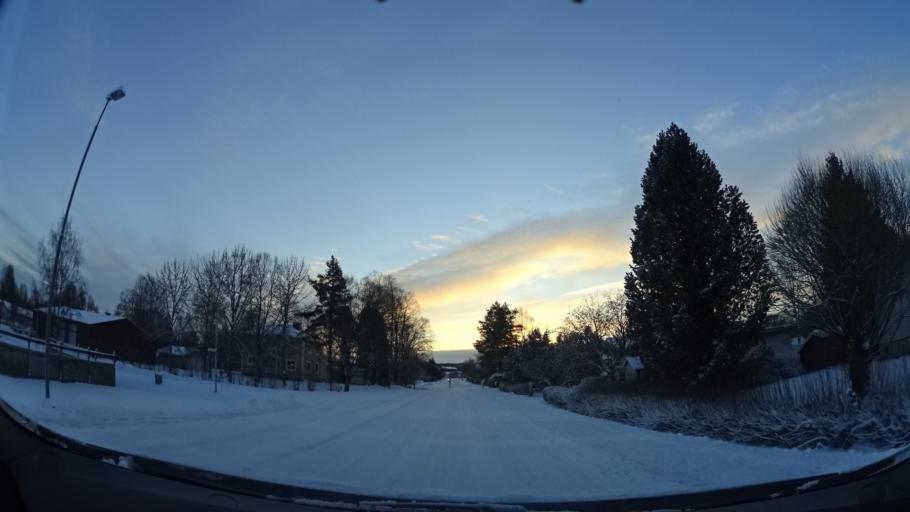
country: SE
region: Vaesterbotten
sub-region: Skelleftea Kommun
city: Kage
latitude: 64.8396
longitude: 20.9852
